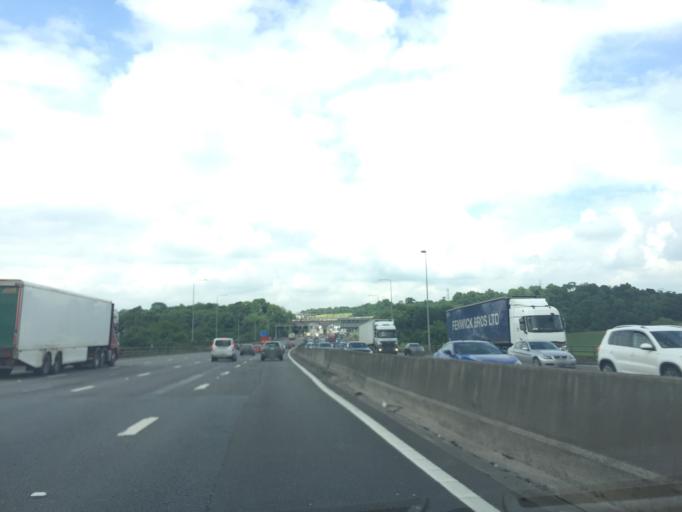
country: GB
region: England
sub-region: Buckinghamshire
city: Gerrards Cross
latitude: 51.5782
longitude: -0.5358
